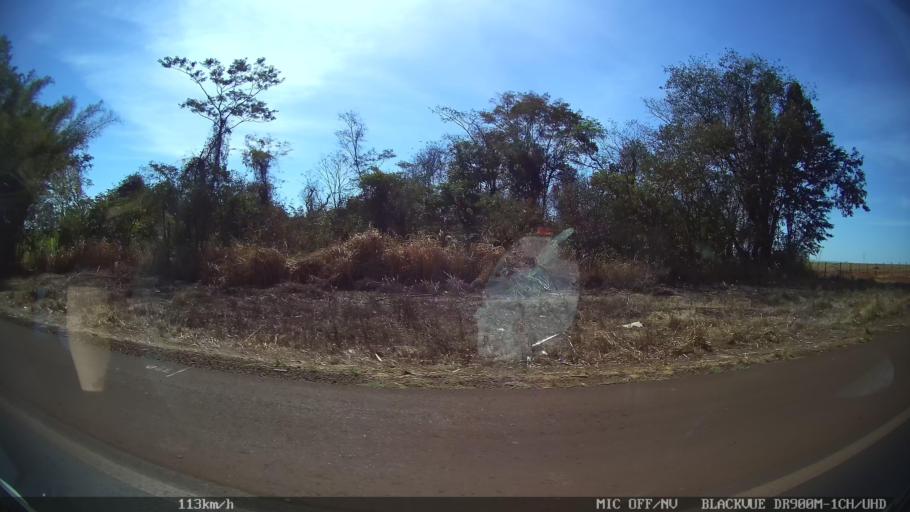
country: BR
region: Sao Paulo
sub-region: Sao Joaquim Da Barra
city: Sao Joaquim da Barra
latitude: -20.5101
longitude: -47.9103
